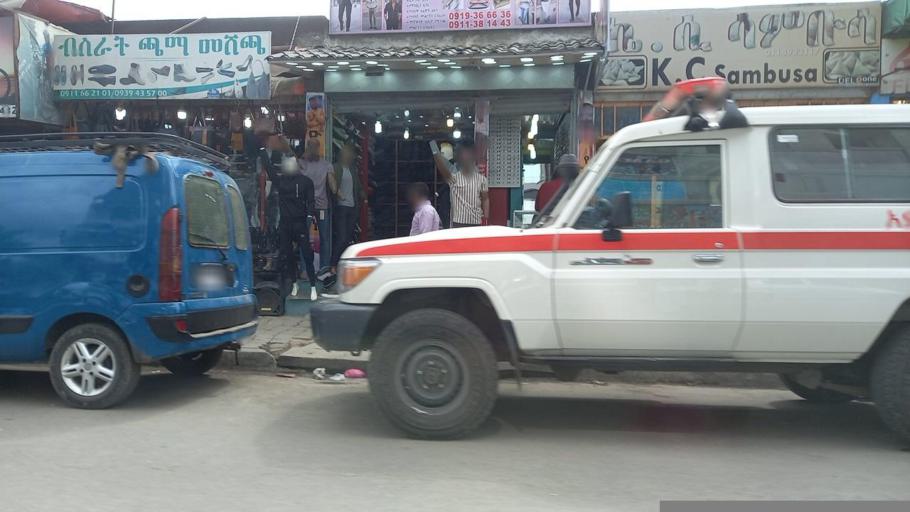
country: ET
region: Adis Abeba
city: Addis Ababa
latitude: 9.0208
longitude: 38.7968
